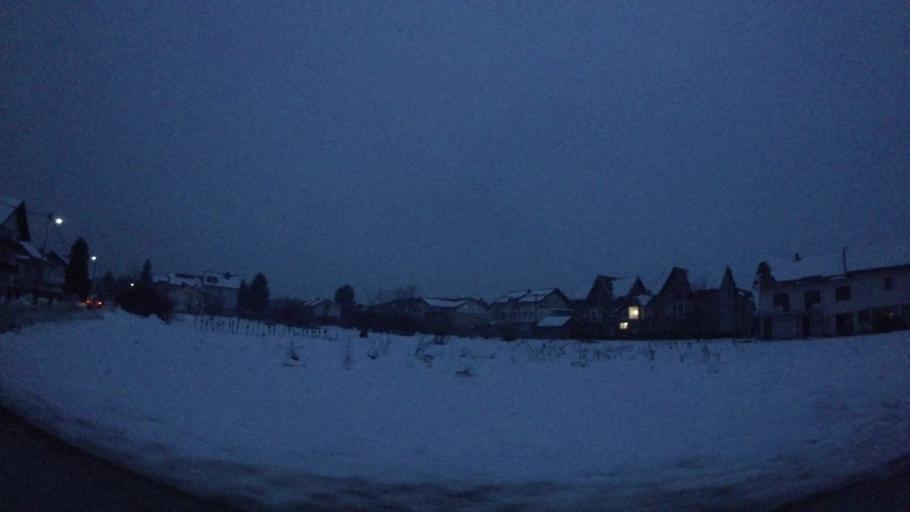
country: BA
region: Federation of Bosnia and Herzegovina
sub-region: Kanton Sarajevo
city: Sarajevo
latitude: 43.8377
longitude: 18.3046
